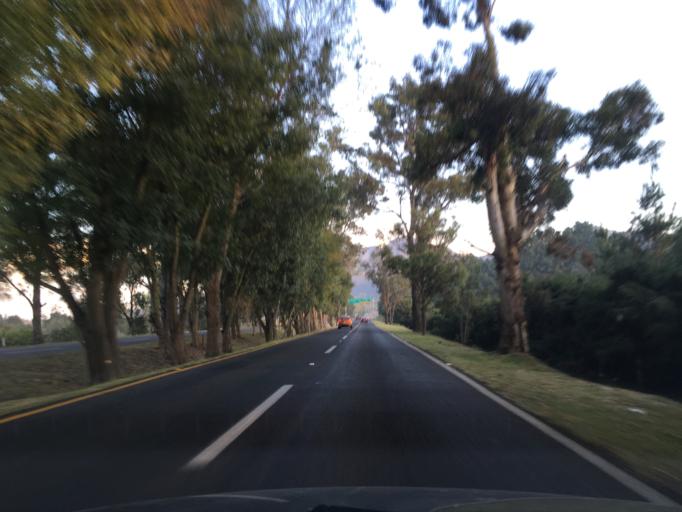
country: MX
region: Michoacan
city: Patzcuaro
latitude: 19.5359
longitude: -101.5718
